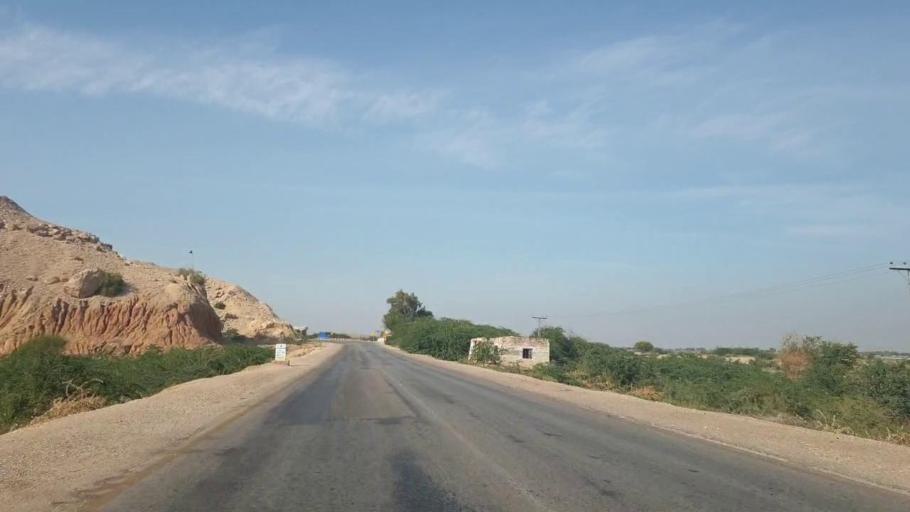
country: PK
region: Sindh
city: Sehwan
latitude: 26.3188
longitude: 67.8885
